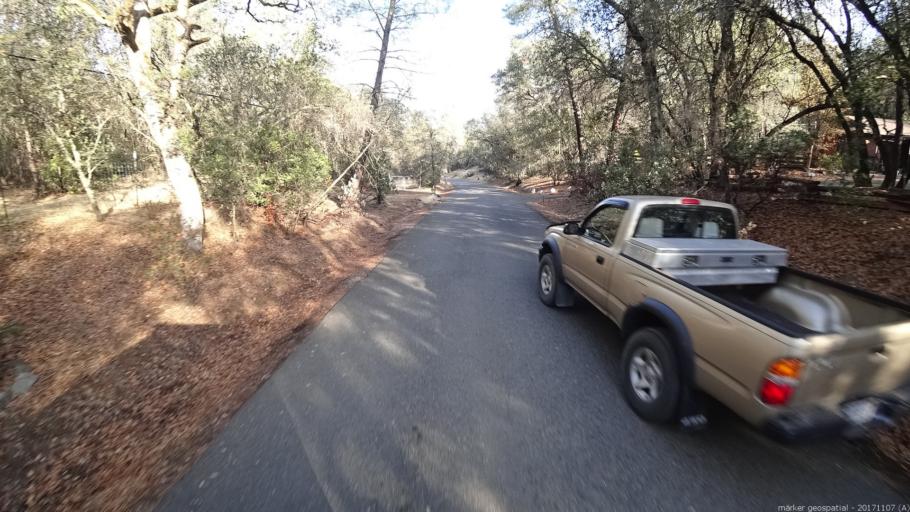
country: US
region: California
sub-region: Shasta County
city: Shasta
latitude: 40.5369
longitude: -122.4557
